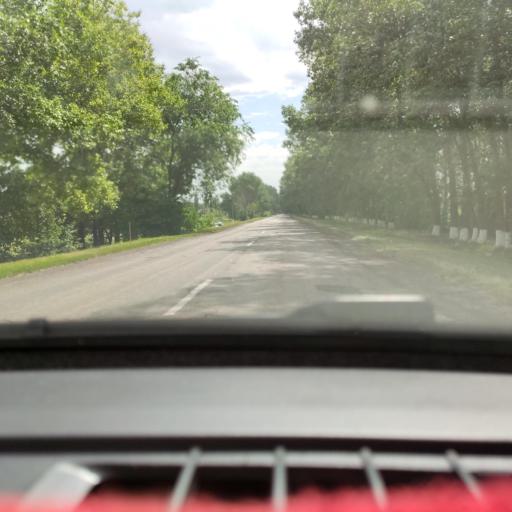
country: RU
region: Voronezj
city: Davydovka
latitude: 51.2459
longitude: 39.5555
